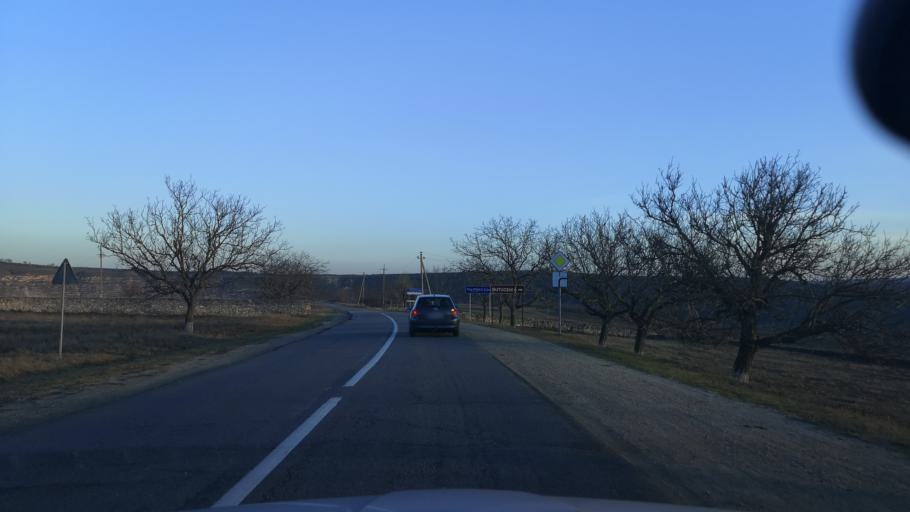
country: MD
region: Telenesti
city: Cocieri
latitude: 47.3094
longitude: 28.9732
